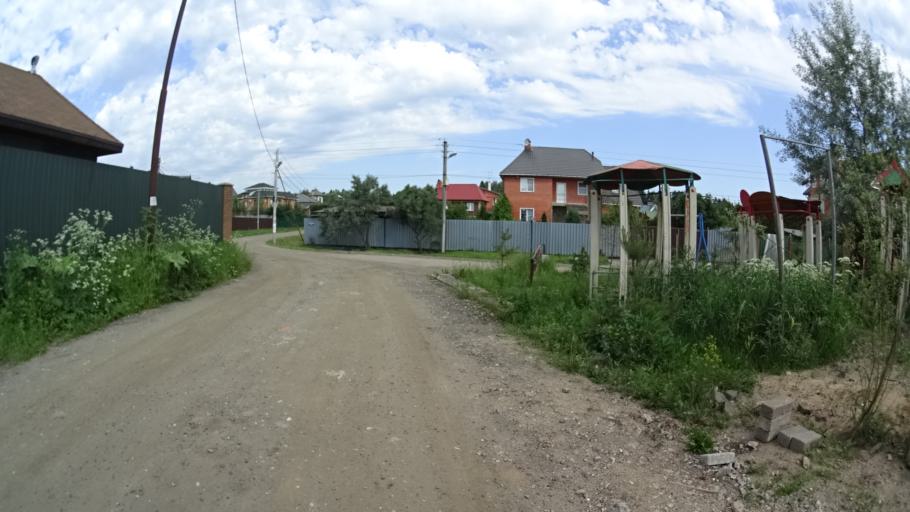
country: RU
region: Moskovskaya
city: Zelenogradskiy
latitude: 56.0911
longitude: 37.9115
